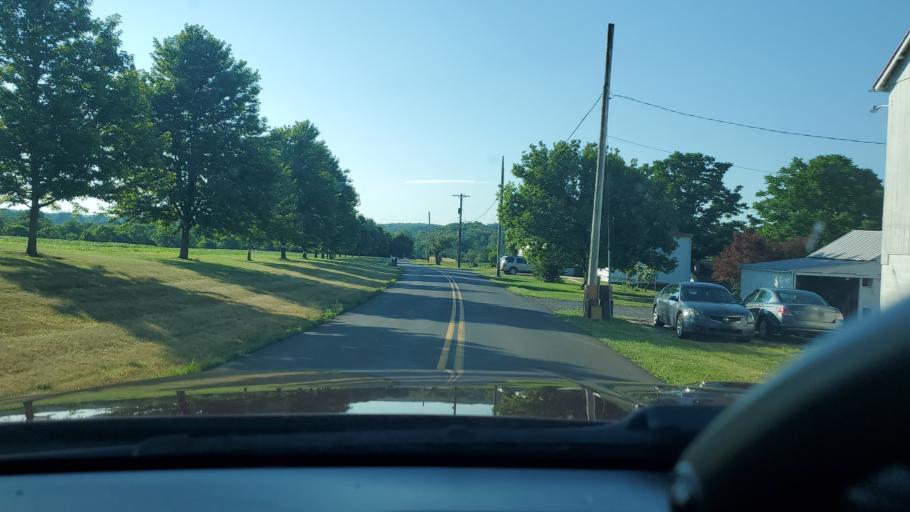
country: US
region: Pennsylvania
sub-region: Montgomery County
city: Harleysville
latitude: 40.3016
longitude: -75.4054
